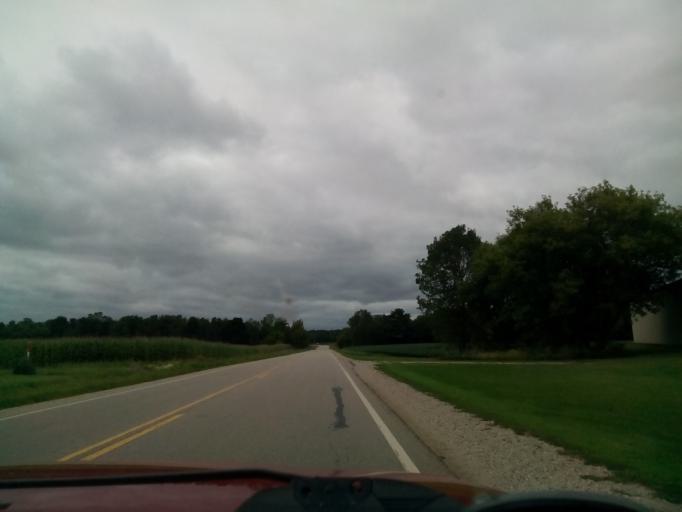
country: US
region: Wisconsin
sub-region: Menominee County
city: Legend Lake
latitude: 44.9993
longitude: -88.4272
